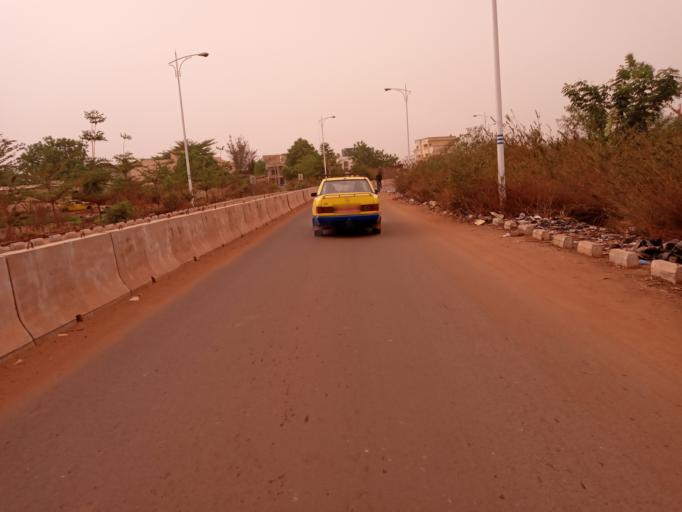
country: ML
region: Bamako
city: Bamako
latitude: 12.6495
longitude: -7.9307
